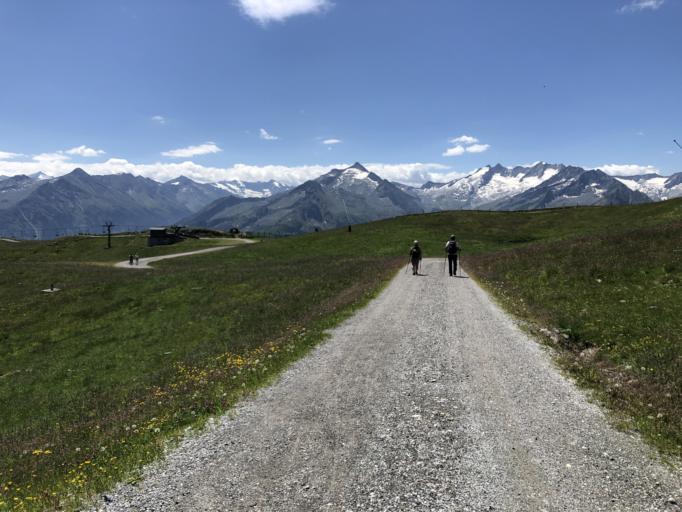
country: AT
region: Salzburg
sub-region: Politischer Bezirk Zell am See
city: Krimml
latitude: 47.2607
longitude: 12.0945
